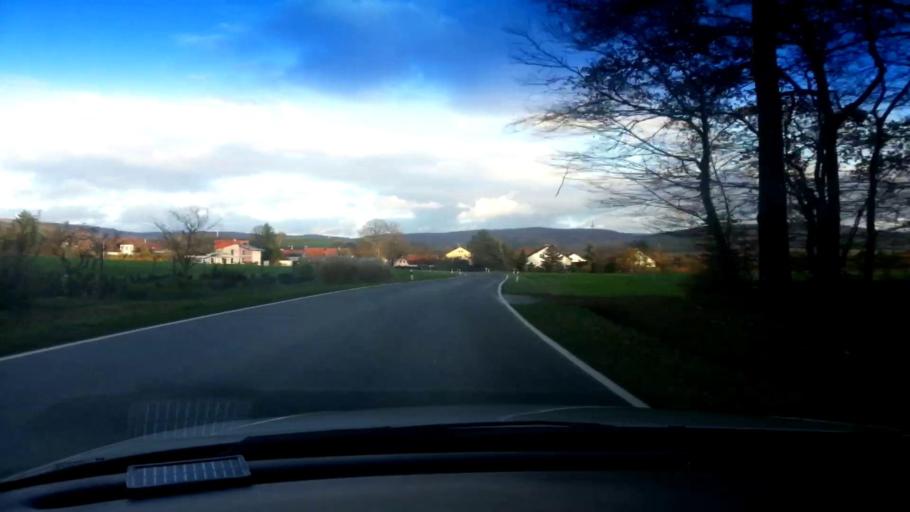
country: DE
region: Bavaria
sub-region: Upper Franconia
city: Strullendorf
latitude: 49.8653
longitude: 10.9891
